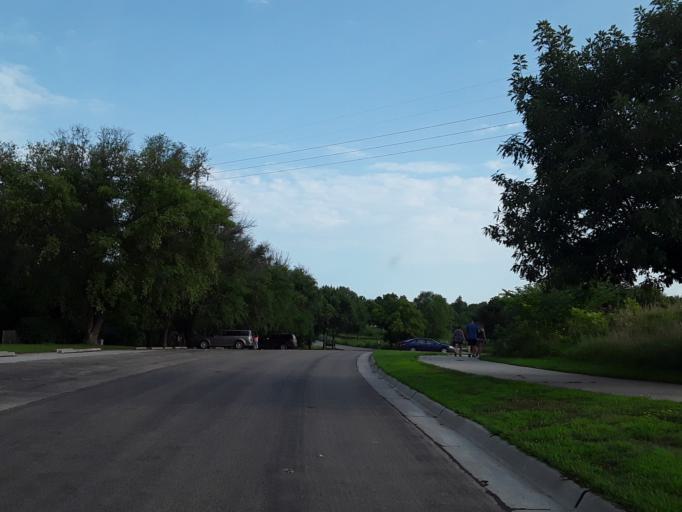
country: US
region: Nebraska
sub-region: Saunders County
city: Ashland
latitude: 41.0221
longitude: -96.3127
